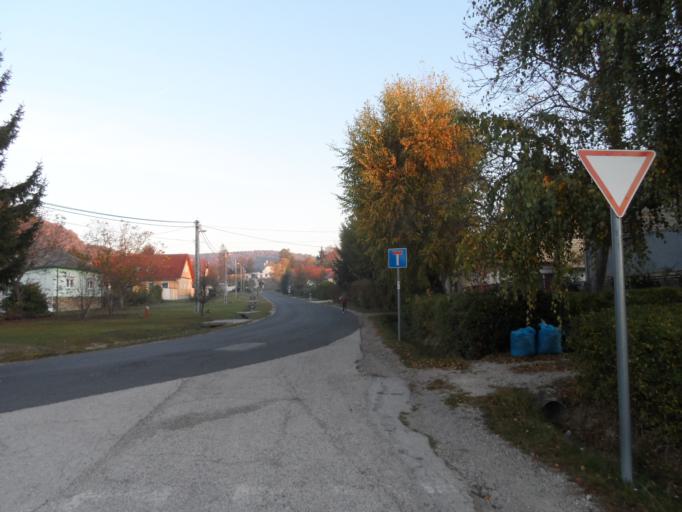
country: HU
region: Veszprem
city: Ajka
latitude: 47.1696
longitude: 17.5475
